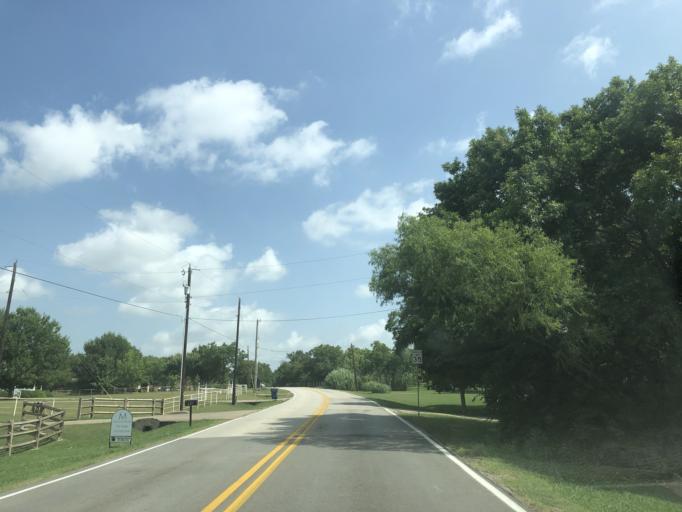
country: US
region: Texas
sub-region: Dallas County
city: Sunnyvale
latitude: 32.8236
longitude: -96.5595
